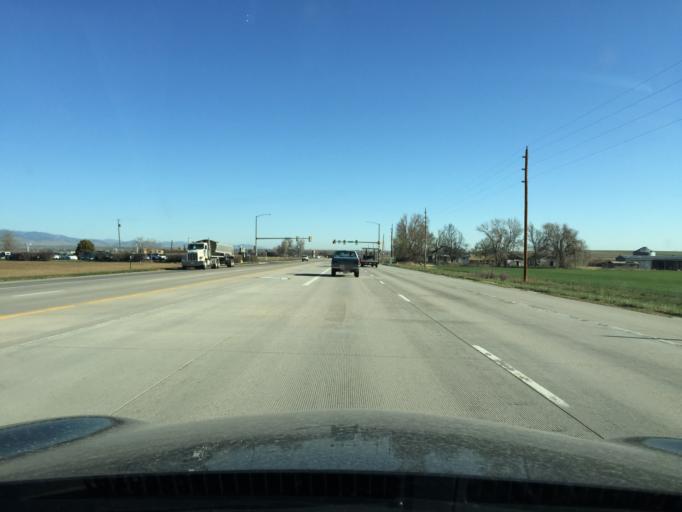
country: US
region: Colorado
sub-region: Boulder County
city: Longmont
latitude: 40.1007
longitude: -105.1028
